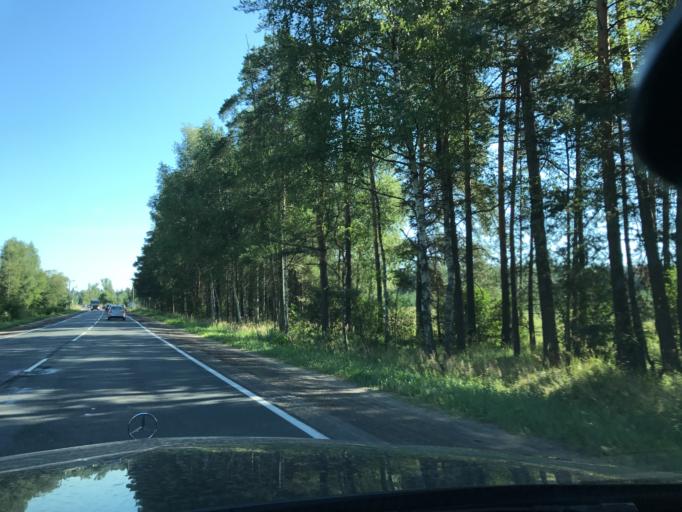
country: RU
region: Vladimir
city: Kirzhach
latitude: 56.1029
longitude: 38.6869
